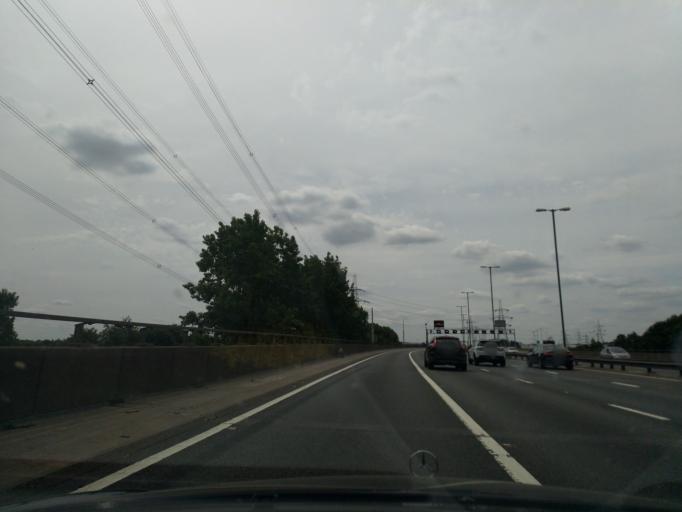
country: GB
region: England
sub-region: City and Borough of Birmingham
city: Acocks Green
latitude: 52.5068
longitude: -1.8193
